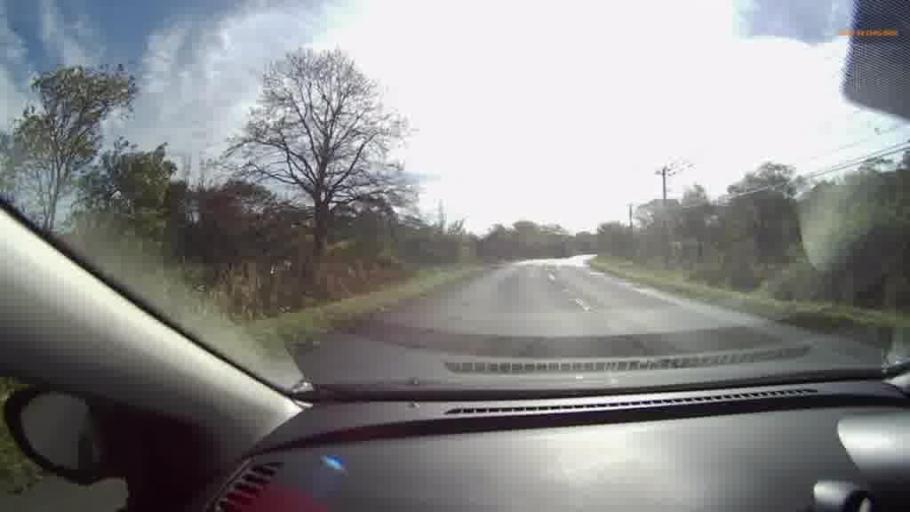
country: JP
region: Hokkaido
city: Kushiro
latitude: 43.0426
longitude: 144.2311
